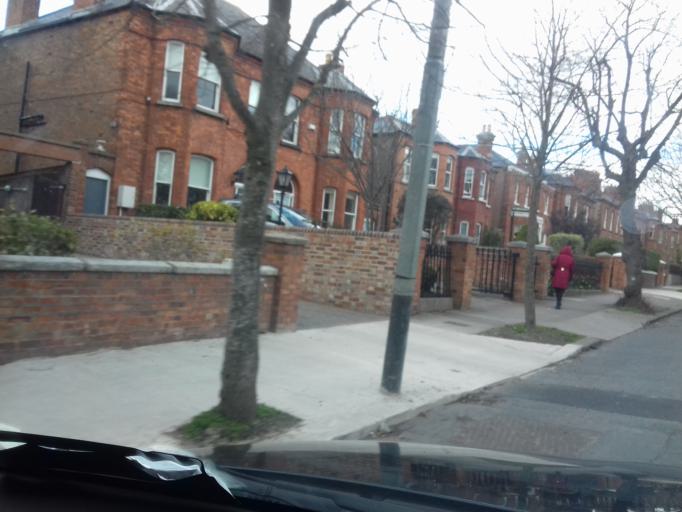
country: IE
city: Donnycarney
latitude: 53.3639
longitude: -6.2150
